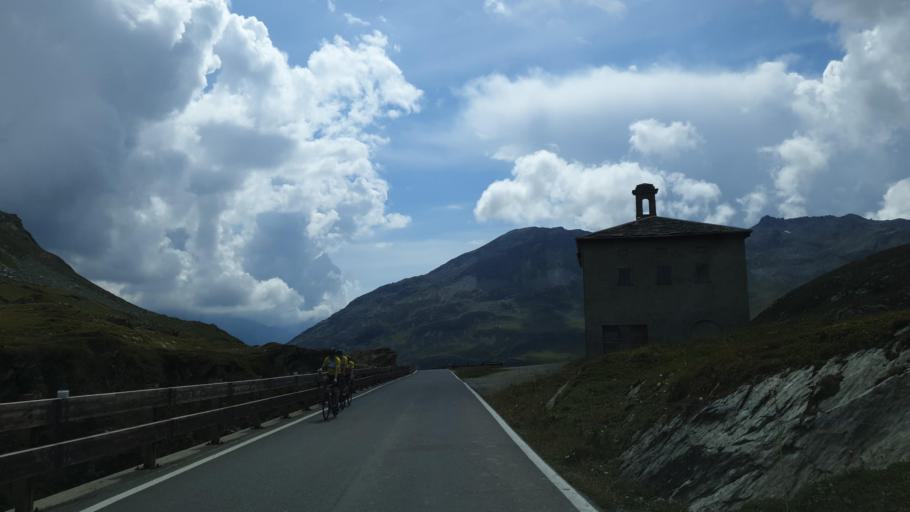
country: IT
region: Lombardy
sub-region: Provincia di Sondrio
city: Campodolcino
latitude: 46.5001
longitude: 9.3298
